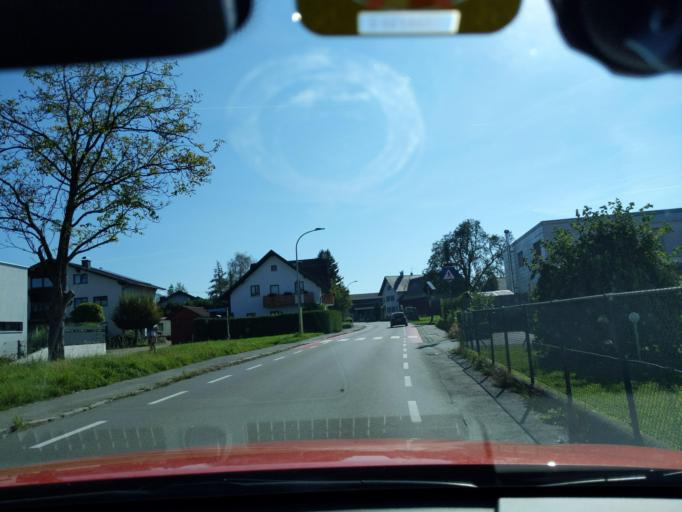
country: AT
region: Vorarlberg
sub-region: Politischer Bezirk Bregenz
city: Horbranz
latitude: 47.5519
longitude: 9.7512
